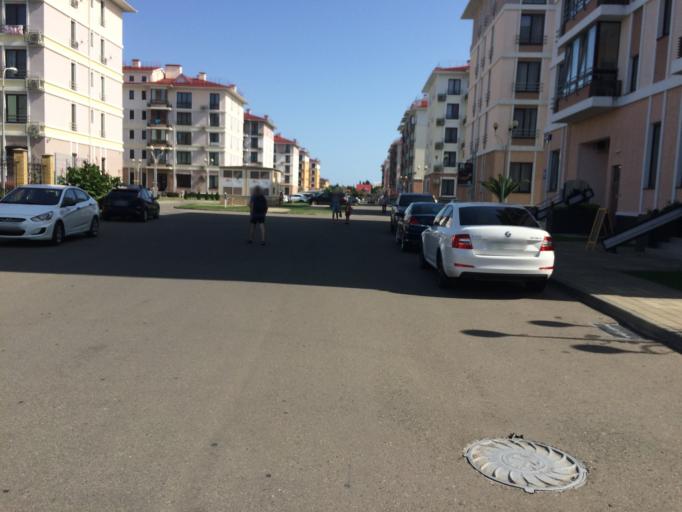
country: RU
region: Krasnodarskiy
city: Adler
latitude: 43.3974
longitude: 39.9754
